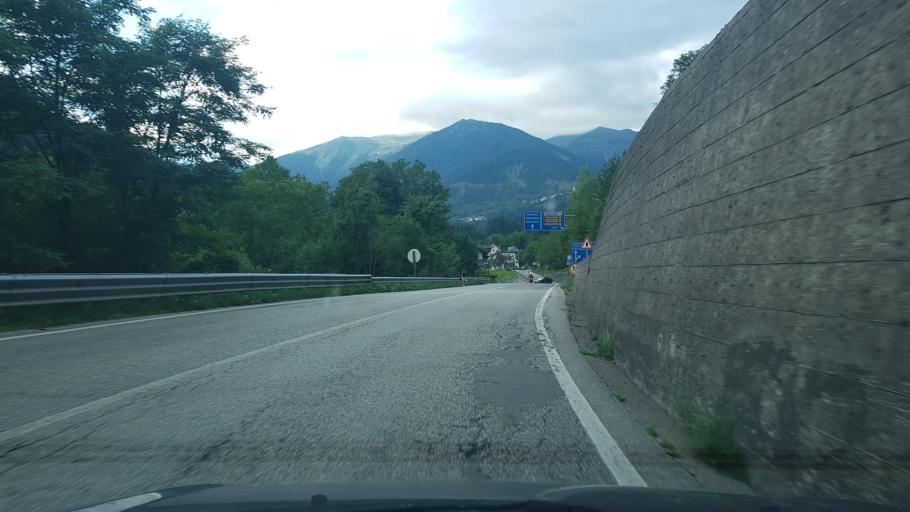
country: IT
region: Friuli Venezia Giulia
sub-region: Provincia di Udine
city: Comeglians
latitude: 46.5090
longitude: 12.8659
